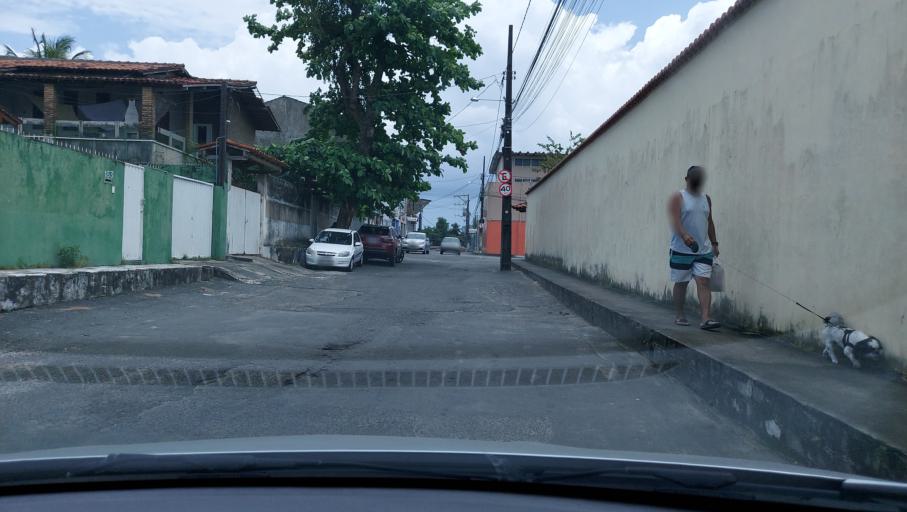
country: BR
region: Bahia
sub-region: Salvador
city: Salvador
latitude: -12.9549
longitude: -38.4606
